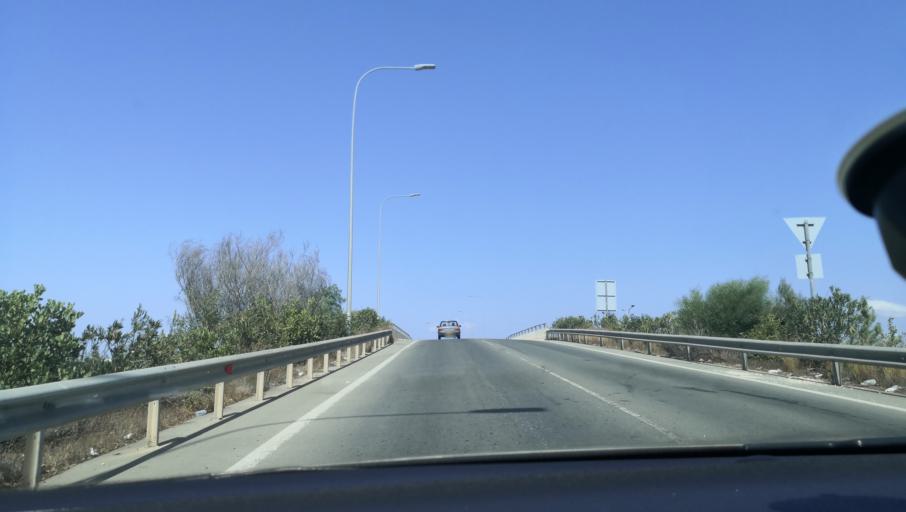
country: CY
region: Lefkosia
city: Kokkinotrimithia
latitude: 35.1598
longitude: 33.2029
